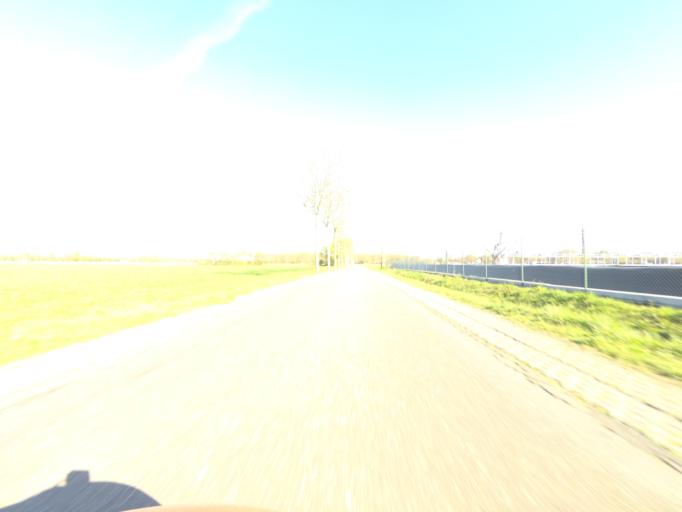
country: NL
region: Gelderland
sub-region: Gemeente Ermelo
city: Horst
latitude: 52.3068
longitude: 5.5676
